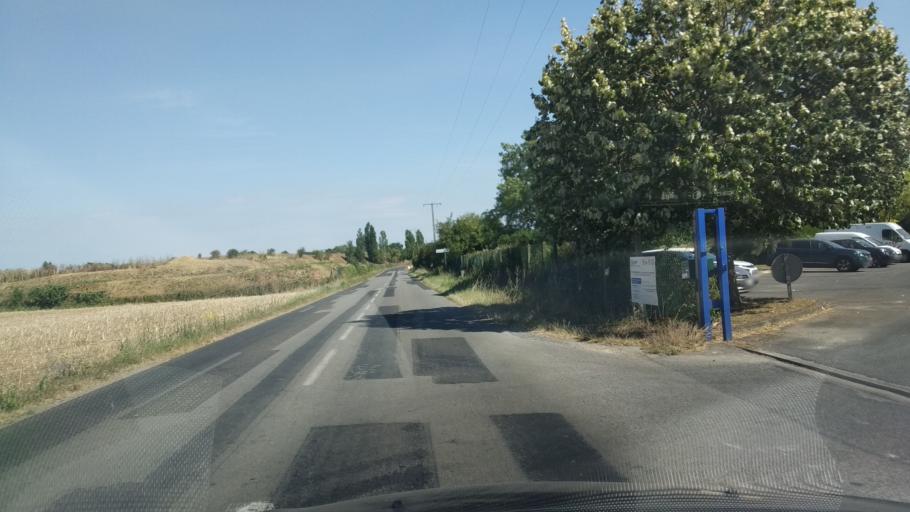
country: FR
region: Poitou-Charentes
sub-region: Departement de la Vienne
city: Cisse
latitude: 46.6630
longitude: 0.2063
